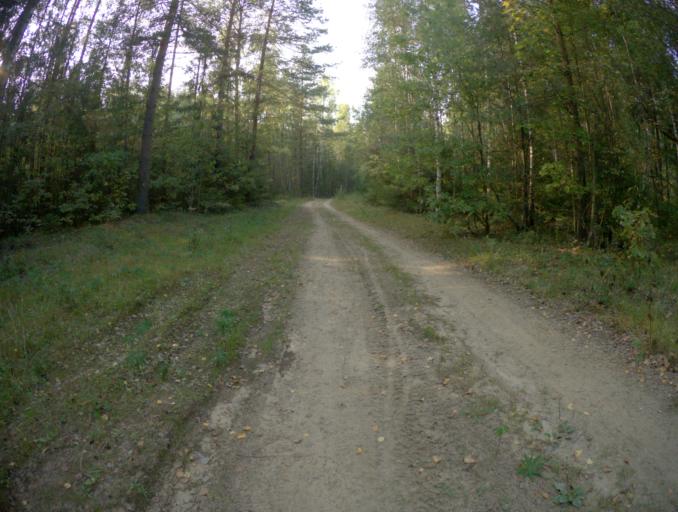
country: RU
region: Vladimir
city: Golovino
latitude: 55.9983
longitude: 40.4507
